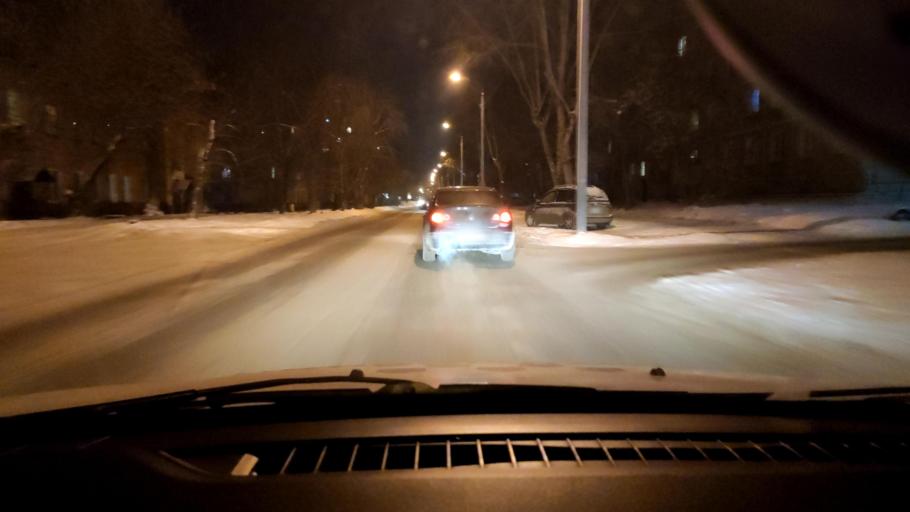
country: RU
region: Perm
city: Kultayevo
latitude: 58.0040
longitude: 55.9487
